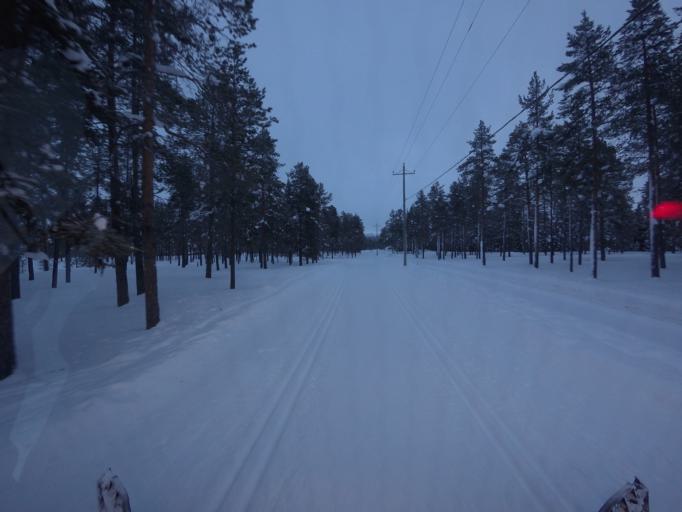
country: FI
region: Lapland
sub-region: Tunturi-Lappi
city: Kolari
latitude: 67.6208
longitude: 24.1709
